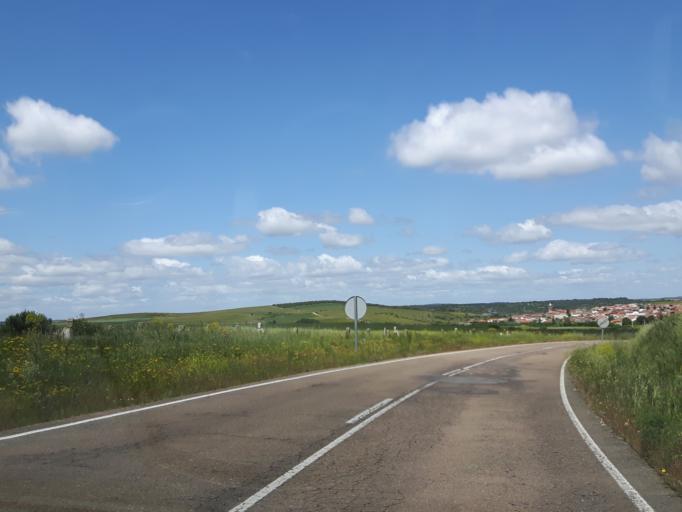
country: ES
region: Castille and Leon
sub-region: Provincia de Salamanca
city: Villar de Ciervo
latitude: 40.7320
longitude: -6.7249
